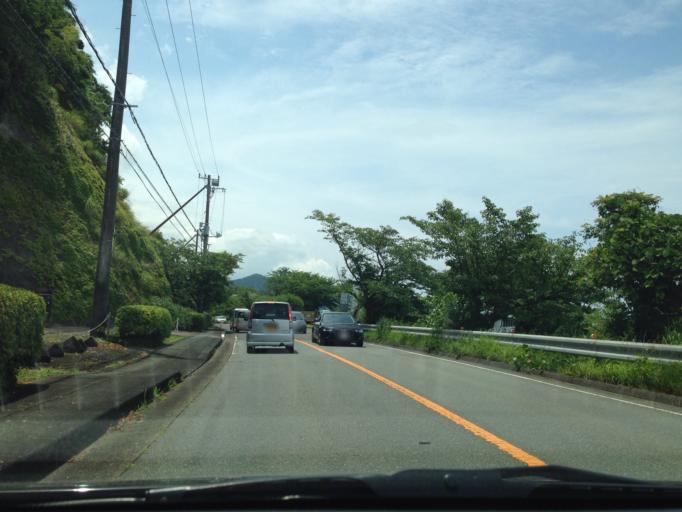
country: JP
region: Shizuoka
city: Heda
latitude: 34.8700
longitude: 138.7614
